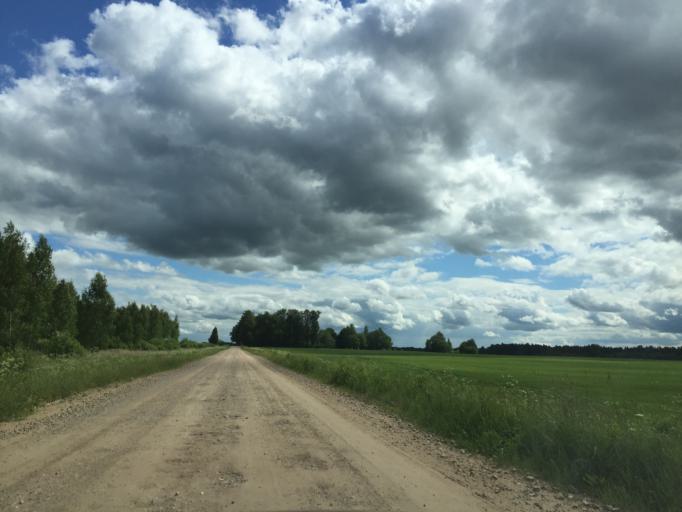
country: LV
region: Vecumnieki
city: Vecumnieki
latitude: 56.4836
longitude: 24.4140
